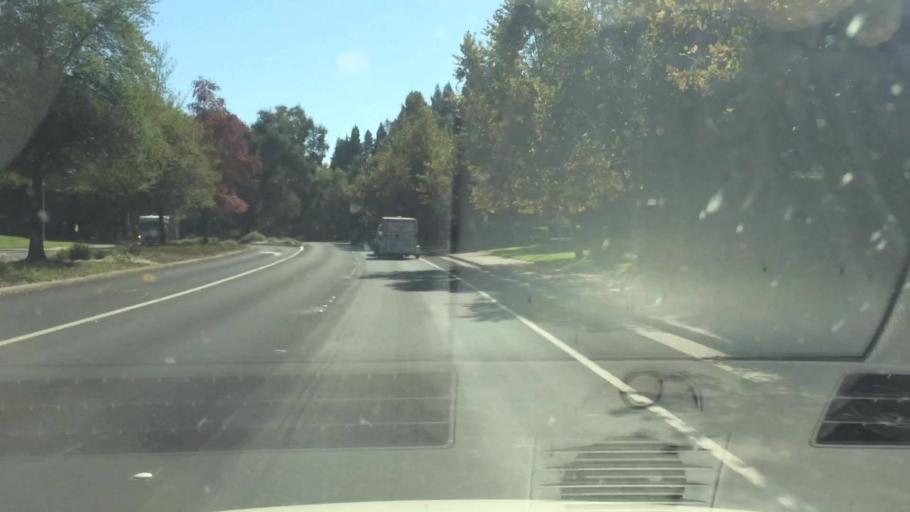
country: US
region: California
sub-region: Sacramento County
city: Citrus Heights
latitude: 38.7330
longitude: -121.2341
